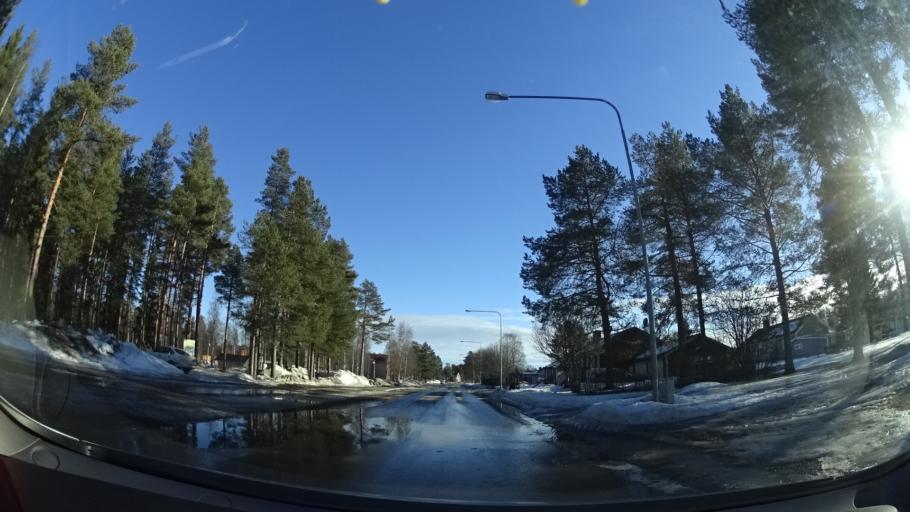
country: SE
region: Vaesterbotten
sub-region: Skelleftea Kommun
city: Byske
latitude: 64.9547
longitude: 21.2128
